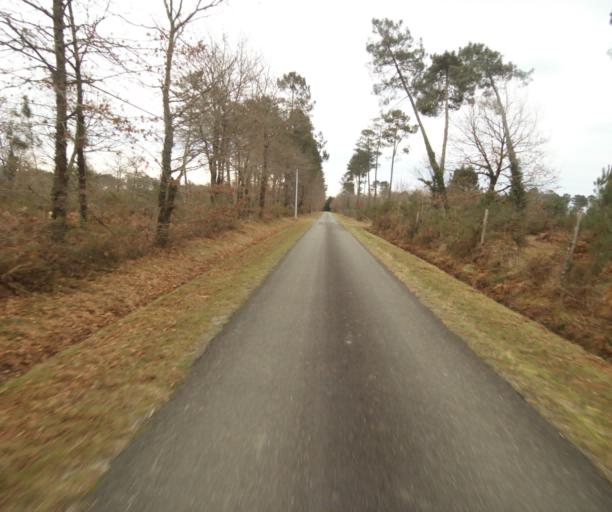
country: FR
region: Midi-Pyrenees
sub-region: Departement du Gers
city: Cazaubon
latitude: 44.0206
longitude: -0.0723
